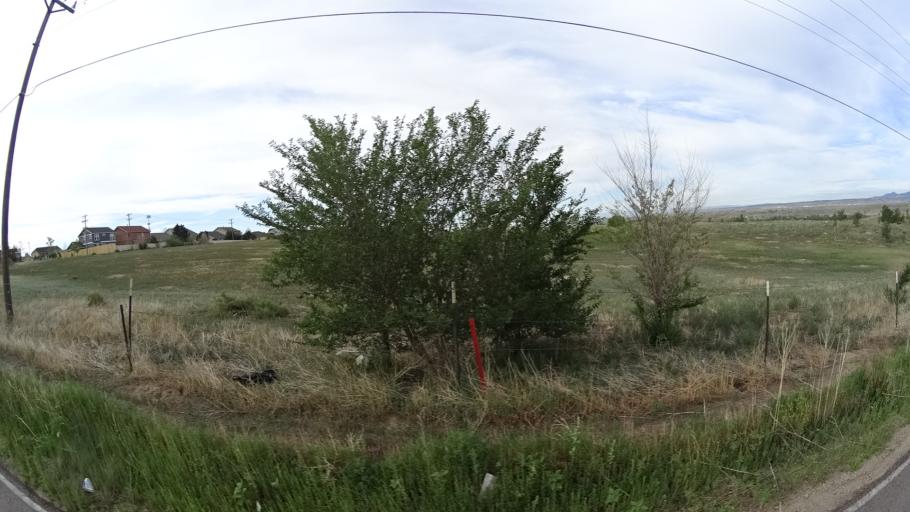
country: US
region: Colorado
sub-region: El Paso County
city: Security-Widefield
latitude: 38.7157
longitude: -104.7039
